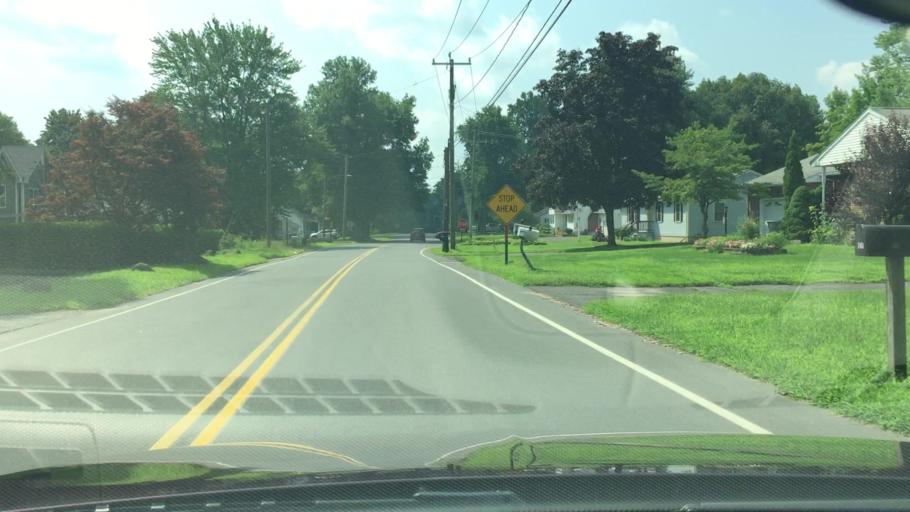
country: US
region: Connecticut
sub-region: Hartford County
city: Plainville
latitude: 41.6589
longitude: -72.8851
